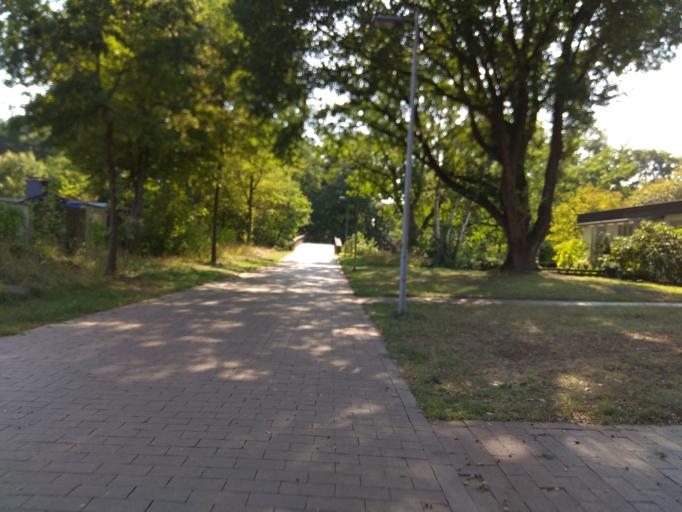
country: DE
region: North Rhine-Westphalia
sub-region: Regierungsbezirk Munster
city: Klein Reken
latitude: 51.7337
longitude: 7.0408
